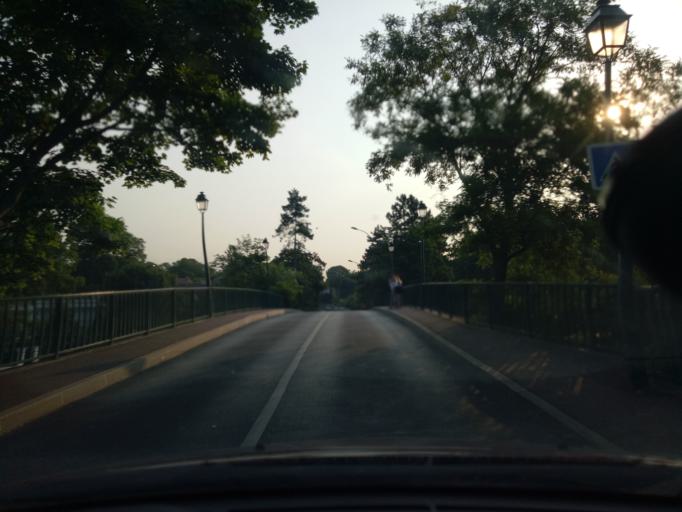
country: FR
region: Ile-de-France
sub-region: Departement des Yvelines
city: Le Vesinet
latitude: 48.8883
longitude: 2.1395
